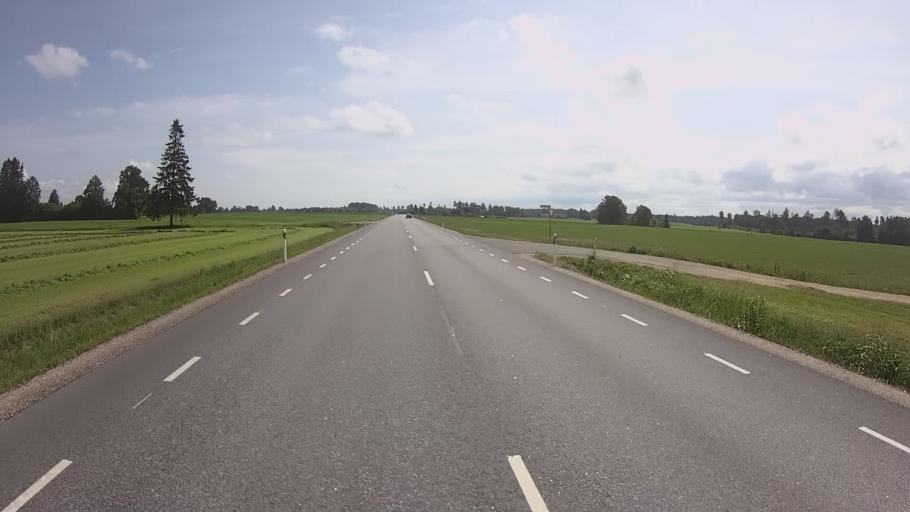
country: EE
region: Tartu
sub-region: UElenurme vald
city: Ulenurme
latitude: 58.1787
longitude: 26.8496
